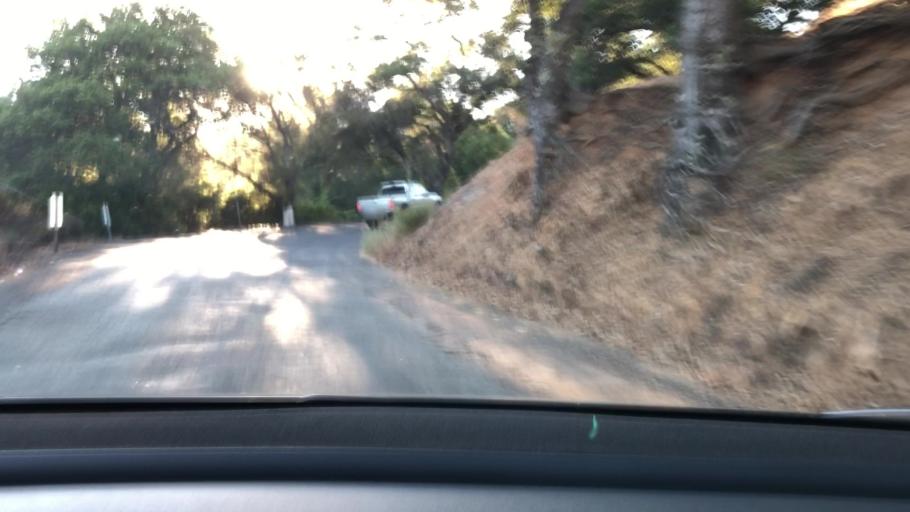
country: US
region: California
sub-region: Santa Clara County
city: Saratoga
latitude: 37.2551
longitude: -122.0616
